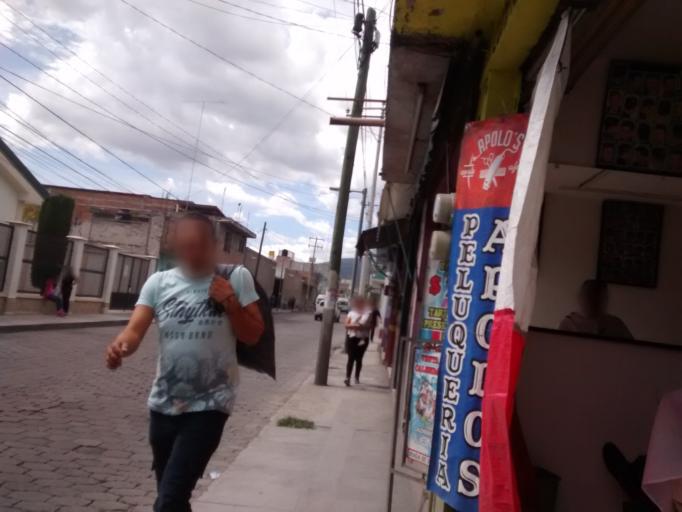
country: MX
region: Puebla
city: Tehuacan
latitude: 18.4589
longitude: -97.3871
